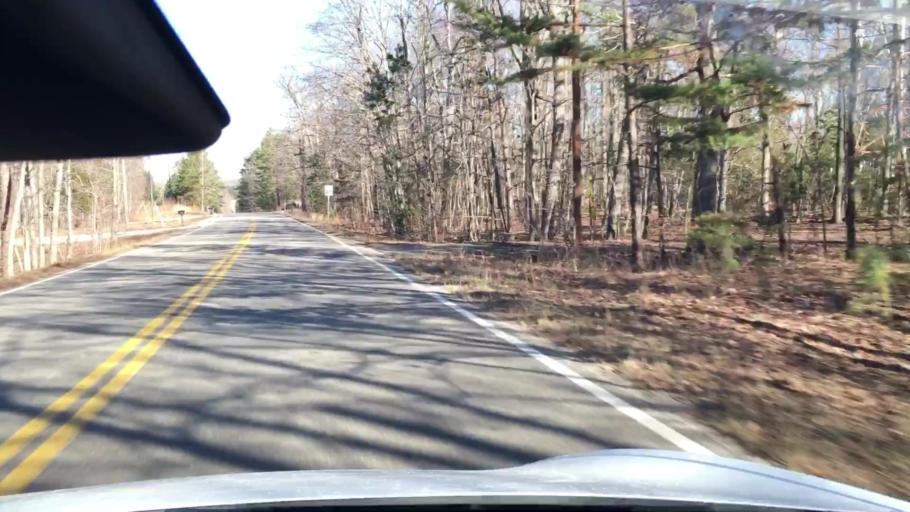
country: US
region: Virginia
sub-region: Powhatan County
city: Powhatan
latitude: 37.5263
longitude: -77.8023
